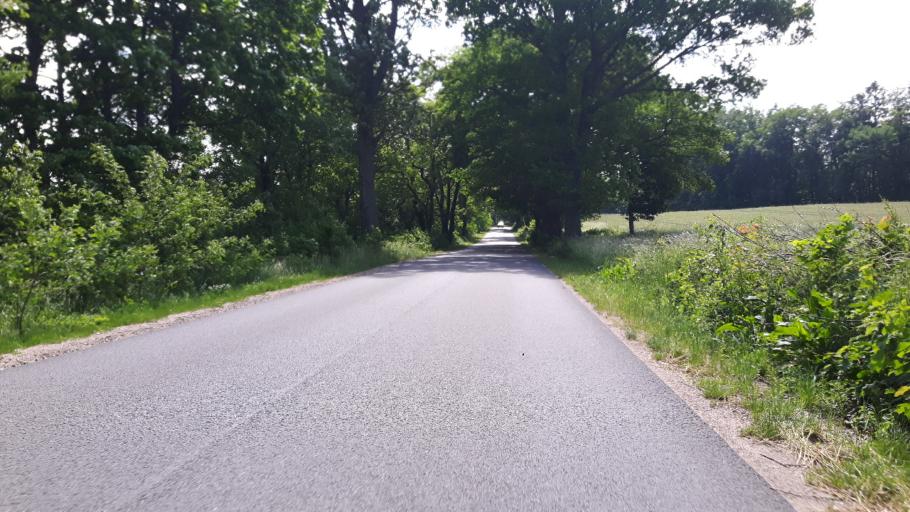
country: PL
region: Pomeranian Voivodeship
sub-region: Powiat wejherowski
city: Choczewo
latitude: 54.7499
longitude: 17.7943
